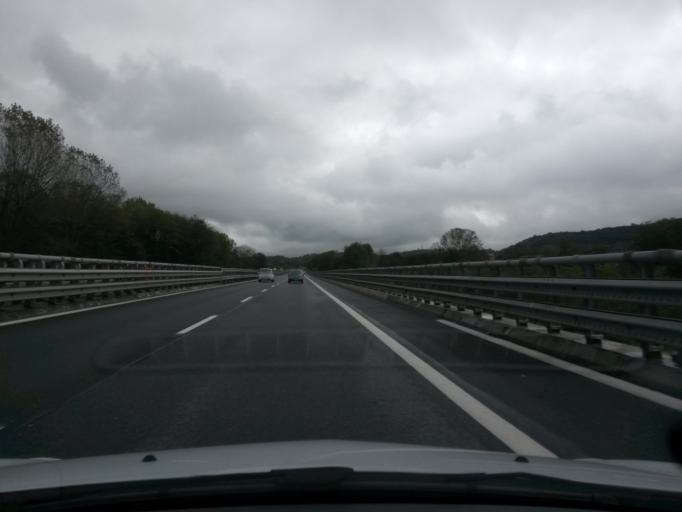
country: IT
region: Piedmont
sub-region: Provincia di Torino
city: Rosta
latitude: 45.0890
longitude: 7.4714
